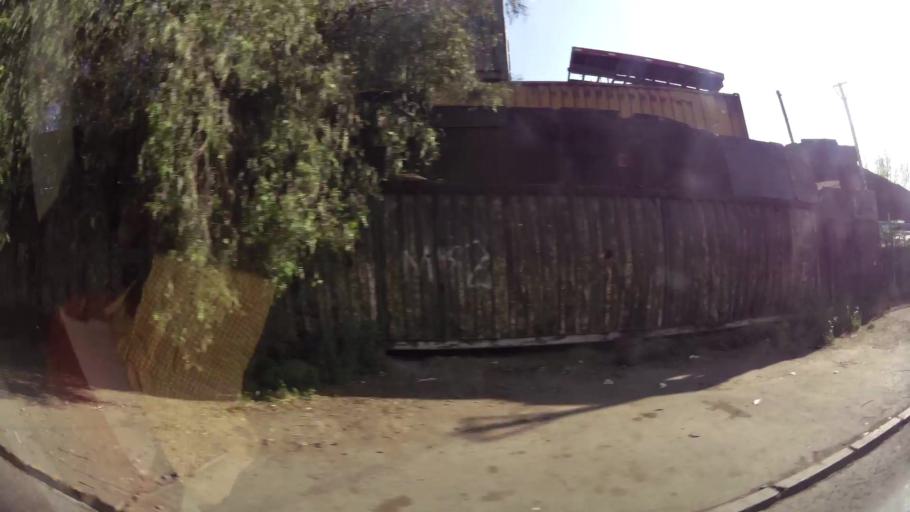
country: CL
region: Santiago Metropolitan
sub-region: Provincia de Santiago
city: Lo Prado
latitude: -33.4141
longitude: -70.7622
